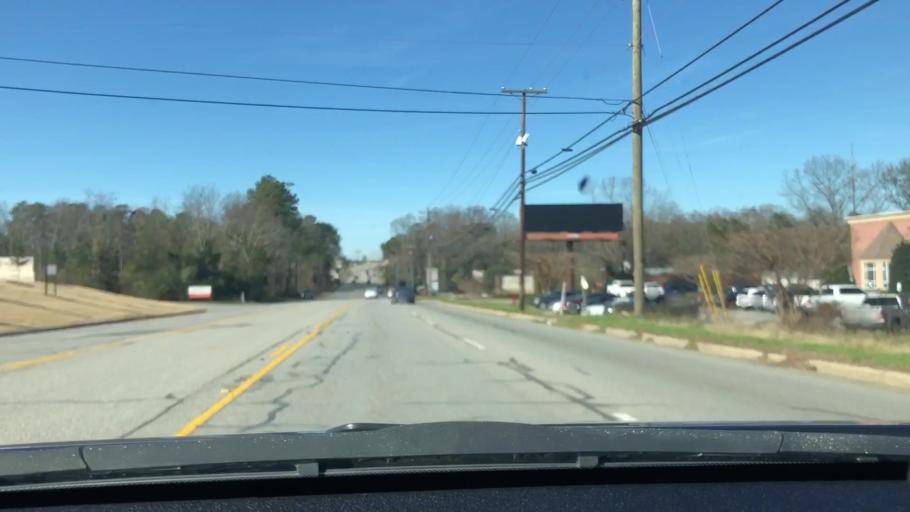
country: US
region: South Carolina
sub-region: Lexington County
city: Oak Grove
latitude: 34.0080
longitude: -81.1334
